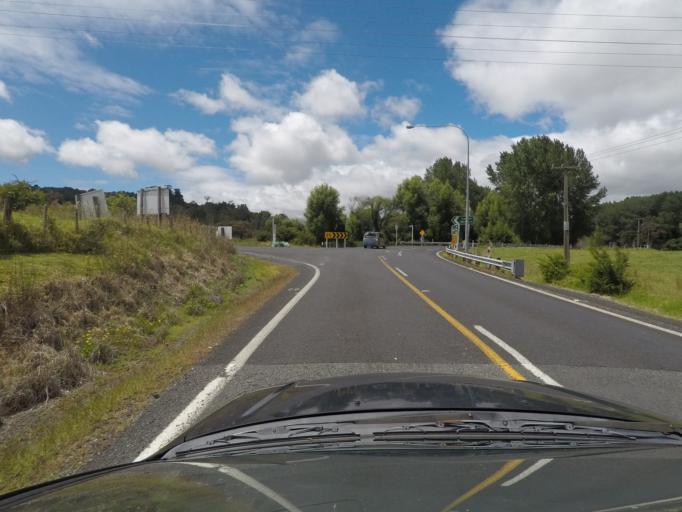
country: NZ
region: Northland
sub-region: Far North District
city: Kawakawa
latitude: -35.3648
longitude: 174.0900
